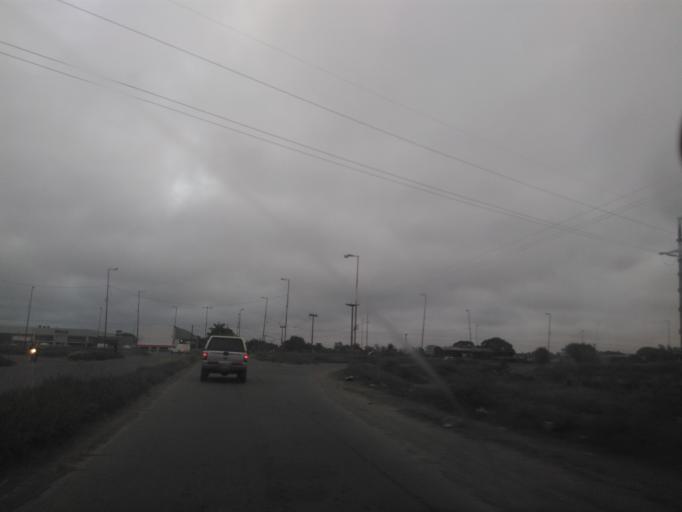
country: AR
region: Chaco
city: Fontana
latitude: -27.4522
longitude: -59.0285
